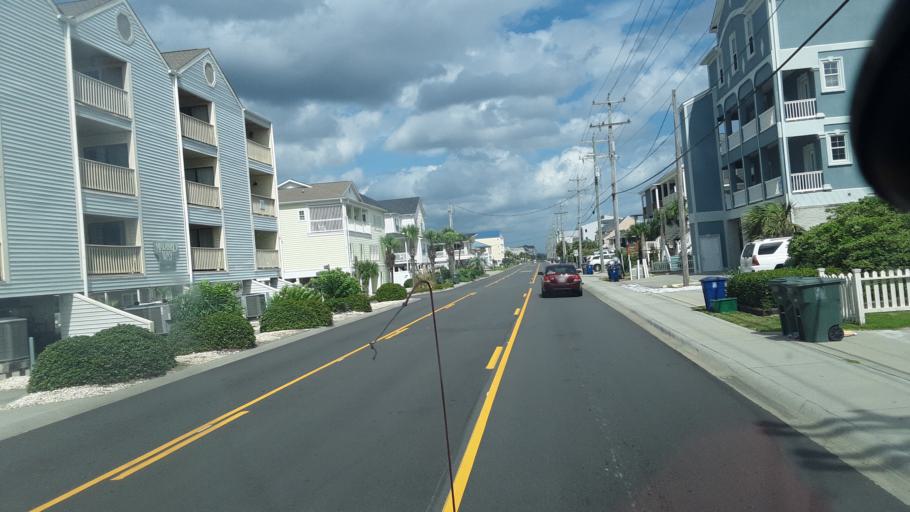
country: US
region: South Carolina
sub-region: Horry County
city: Little River
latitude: 33.8337
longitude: -78.6254
